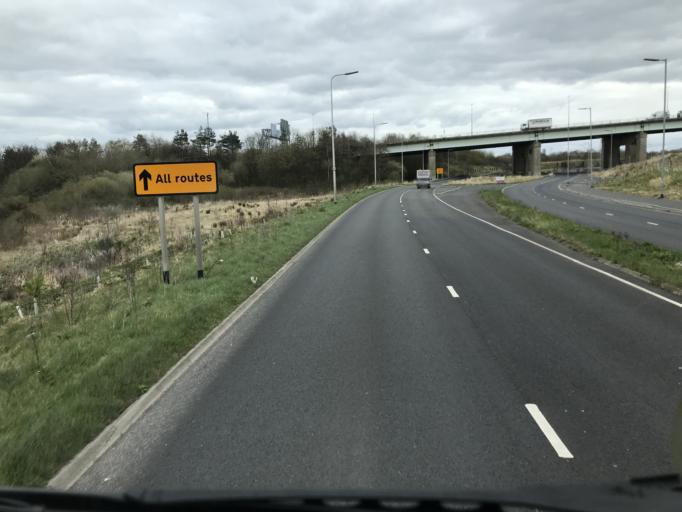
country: GB
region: England
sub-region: Trafford
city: Urmston
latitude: 53.4722
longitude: -2.3751
